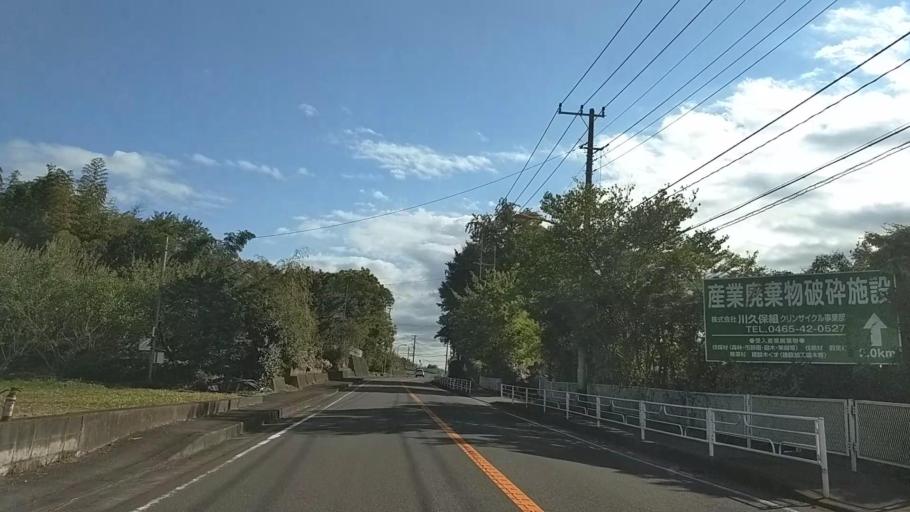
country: JP
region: Kanagawa
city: Odawara
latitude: 35.3103
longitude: 139.1777
